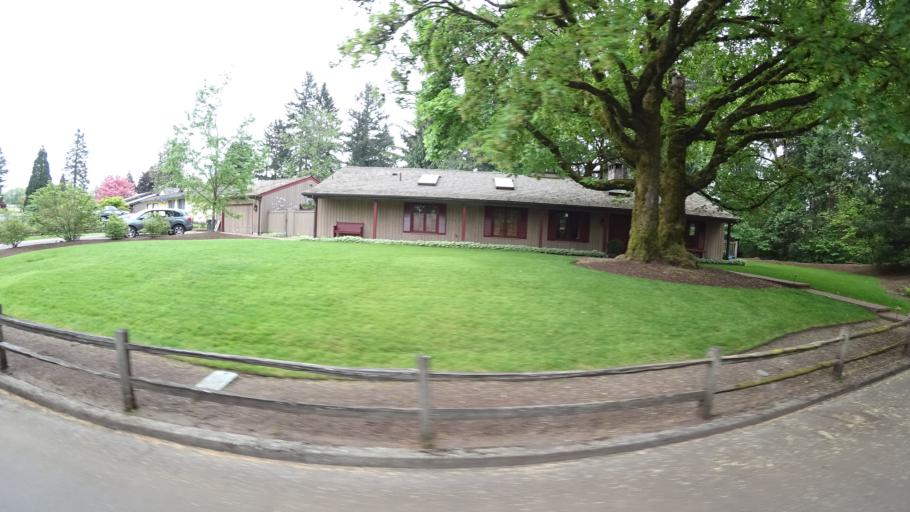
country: US
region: Oregon
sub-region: Washington County
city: Aloha
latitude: 45.5120
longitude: -122.8713
